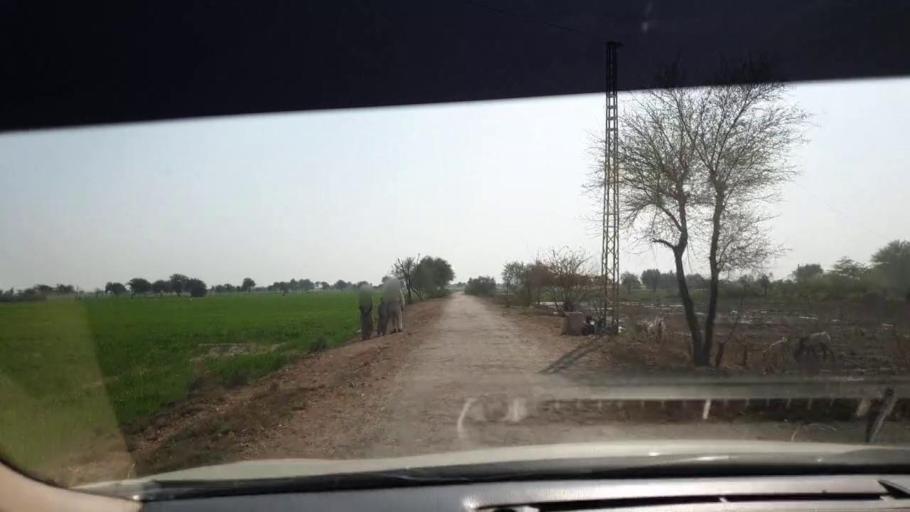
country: PK
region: Sindh
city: Berani
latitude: 25.8110
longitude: 68.7577
